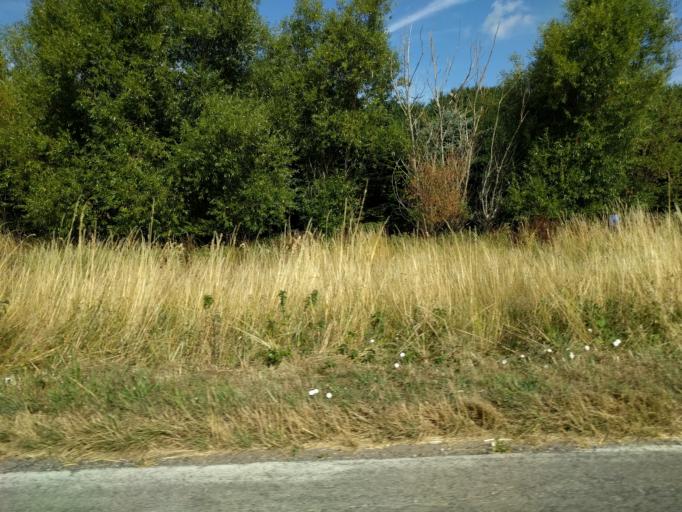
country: DK
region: Zealand
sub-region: Vordingborg Kommune
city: Stege
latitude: 54.9709
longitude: 12.3025
